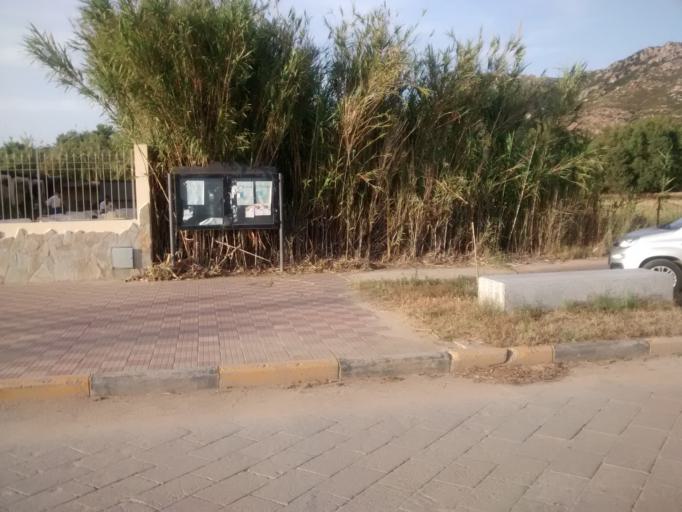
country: IT
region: Sardinia
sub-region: Provincia di Cagliari
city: Villasimius
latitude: 39.1345
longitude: 9.4305
